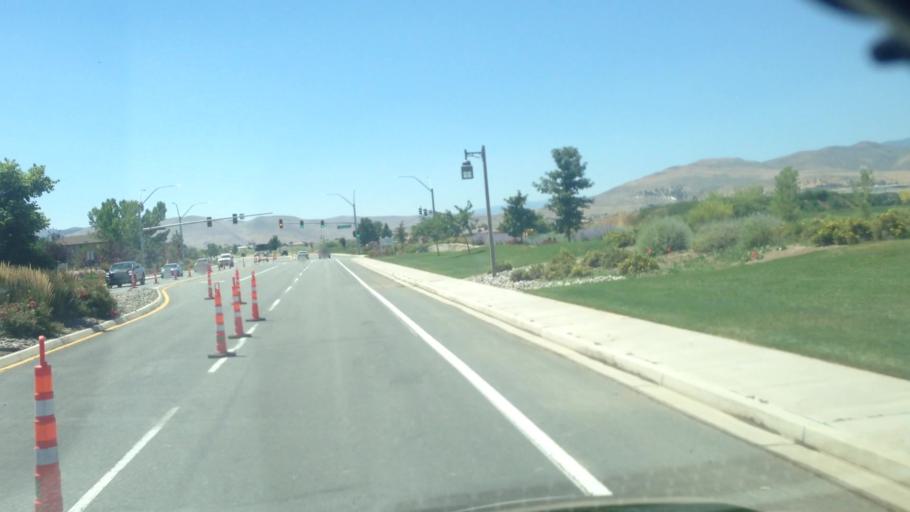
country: US
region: Nevada
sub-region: Washoe County
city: Sparks
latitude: 39.4179
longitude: -119.7328
